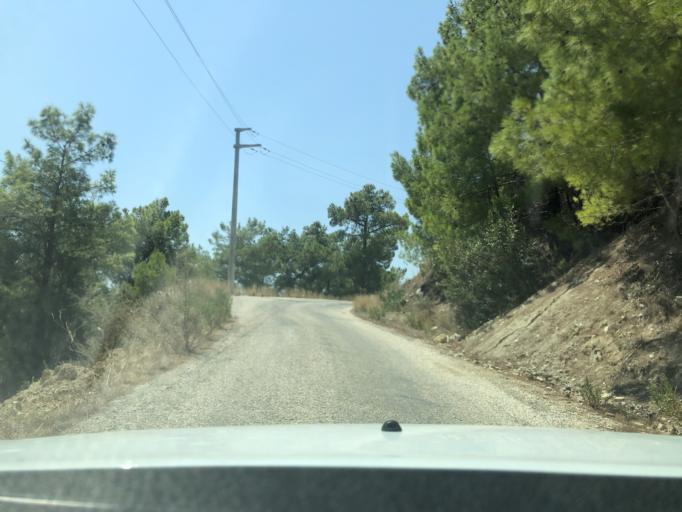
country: TR
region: Antalya
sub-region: Manavgat
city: Manavgat
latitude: 36.8705
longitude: 31.5547
